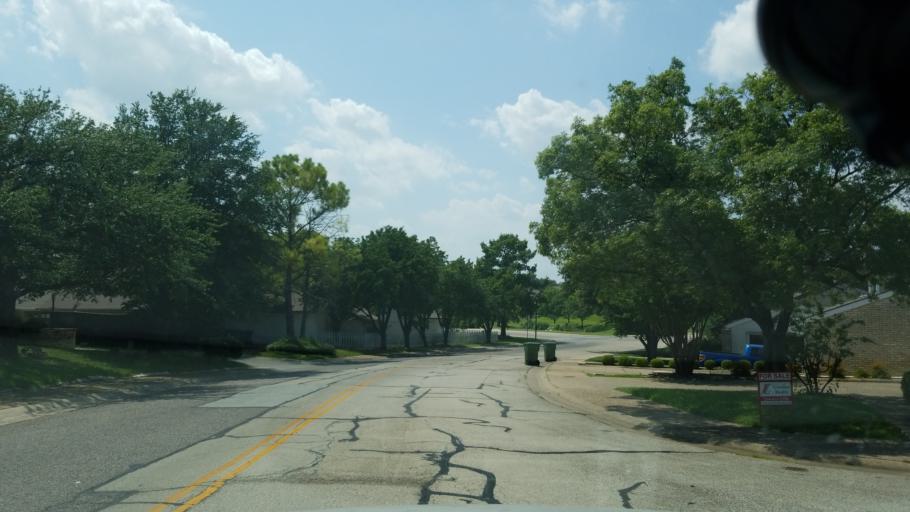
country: US
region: Texas
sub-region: Dallas County
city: Carrollton
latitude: 32.9606
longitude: -96.8603
